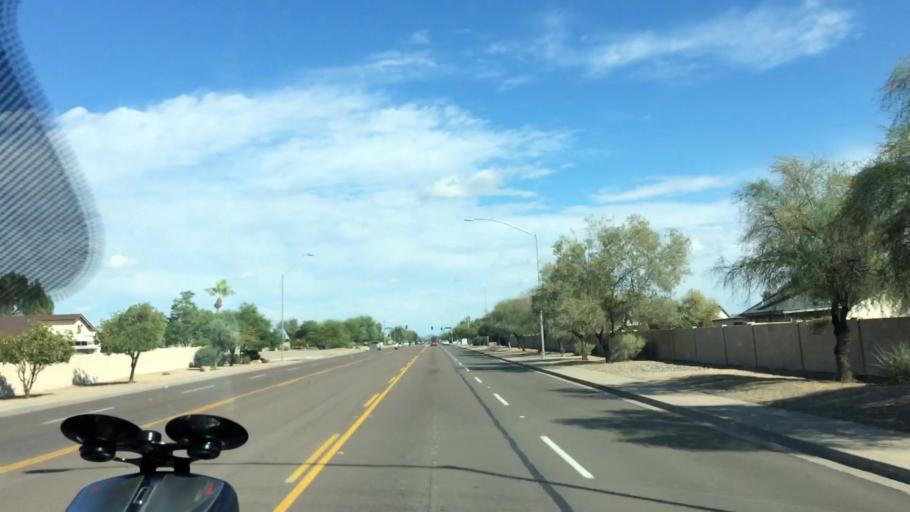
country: US
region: Arizona
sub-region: Maricopa County
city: Peoria
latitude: 33.5664
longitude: -112.2497
